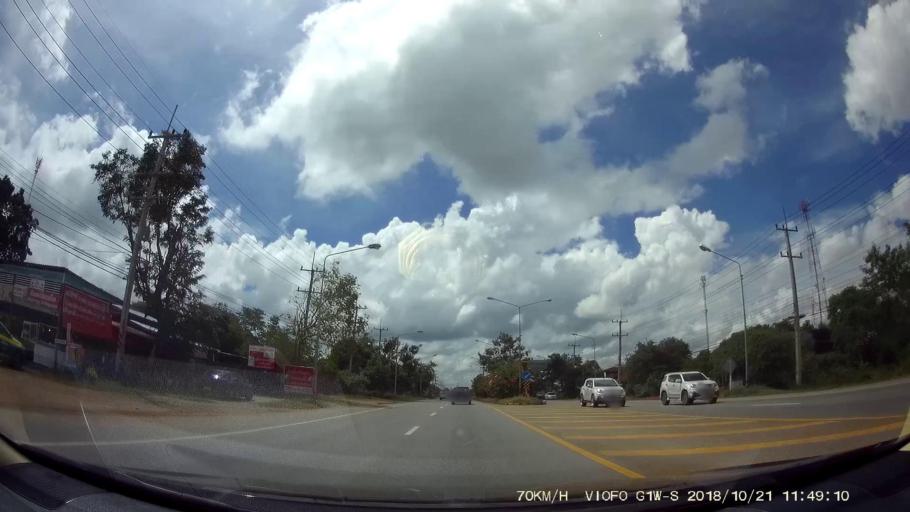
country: TH
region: Chaiyaphum
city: Noen Sa-nga
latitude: 15.6411
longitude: 101.9436
